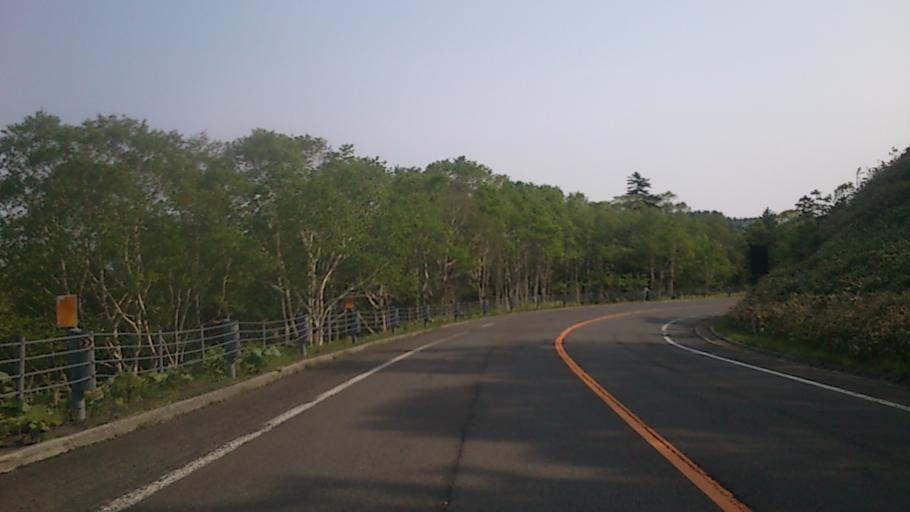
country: JP
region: Hokkaido
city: Bihoro
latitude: 43.4560
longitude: 144.2210
